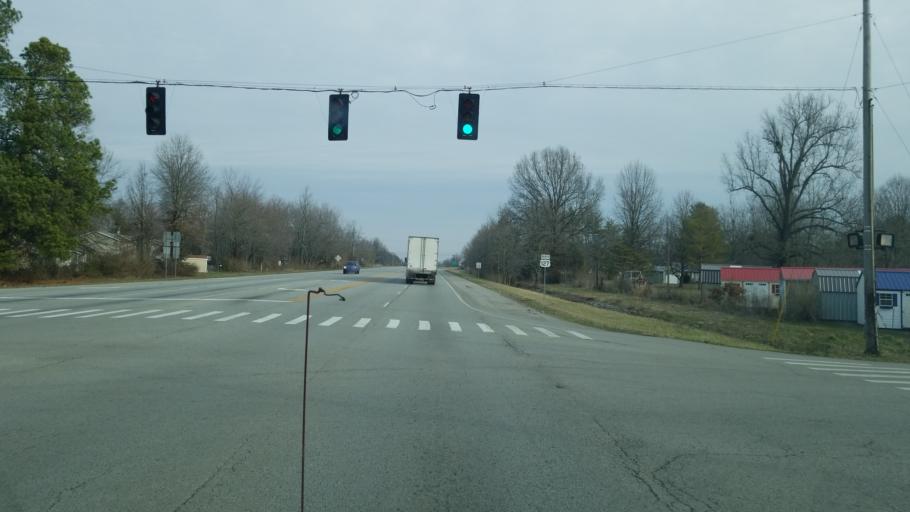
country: US
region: Kentucky
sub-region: Boyle County
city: Junction City
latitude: 37.5828
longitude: -84.7865
